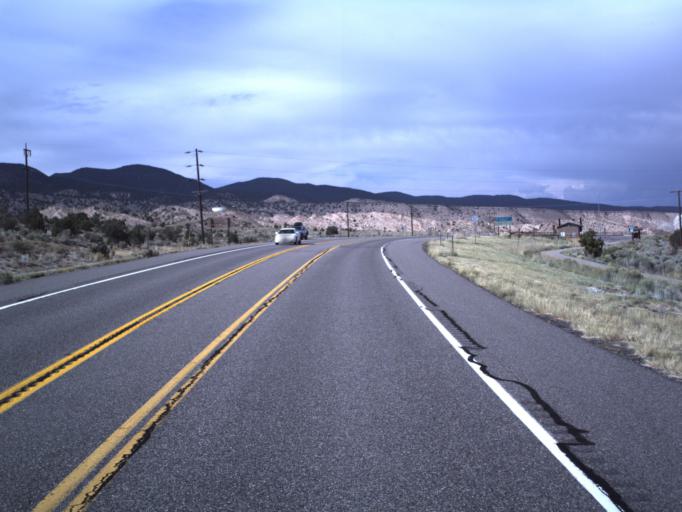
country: US
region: Utah
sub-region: Sevier County
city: Monroe
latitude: 38.5870
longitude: -112.2588
